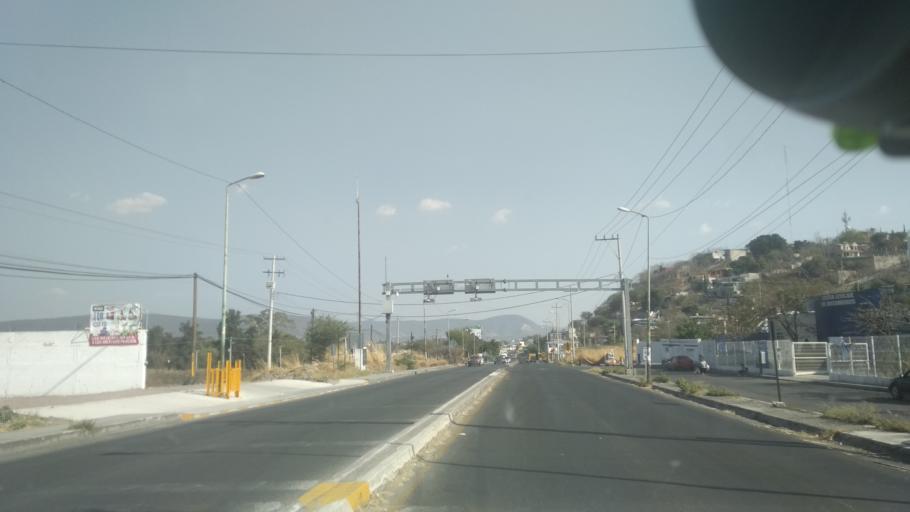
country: MX
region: Puebla
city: Izucar de Matamoros
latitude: 18.6169
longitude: -98.4688
